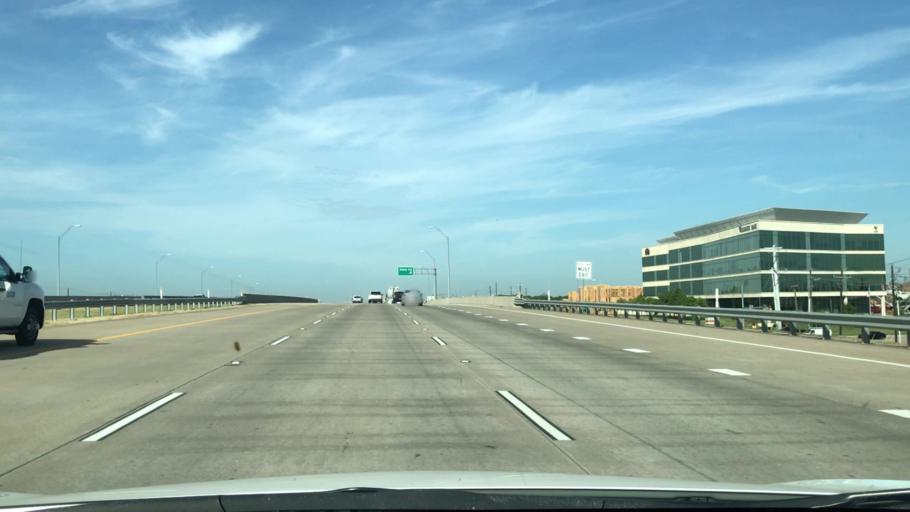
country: US
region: Texas
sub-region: Collin County
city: Allen
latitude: 33.1453
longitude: -96.6780
